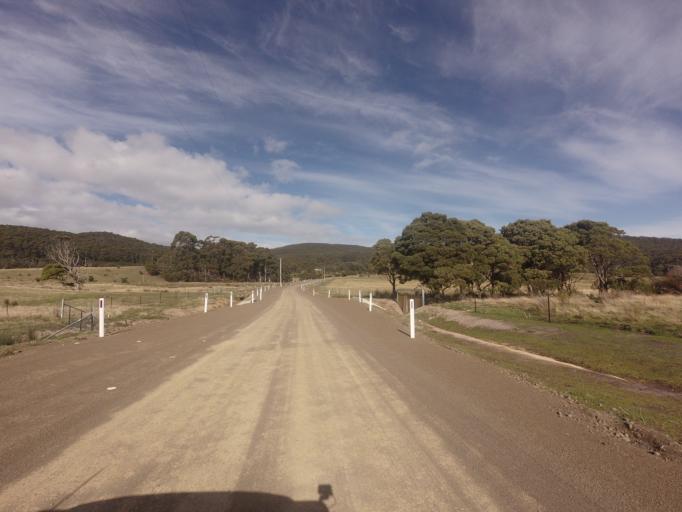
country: AU
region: Tasmania
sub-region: Clarence
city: Sandford
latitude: -43.1908
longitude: 147.7767
